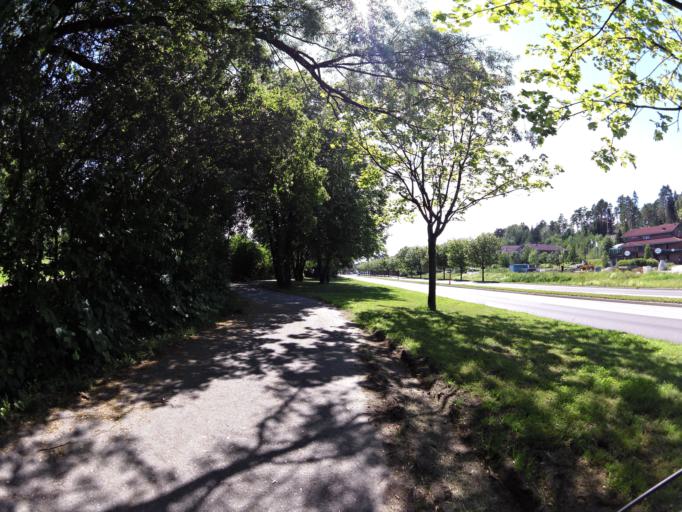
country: NO
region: Ostfold
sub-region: Fredrikstad
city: Fredrikstad
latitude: 59.2282
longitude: 10.9567
